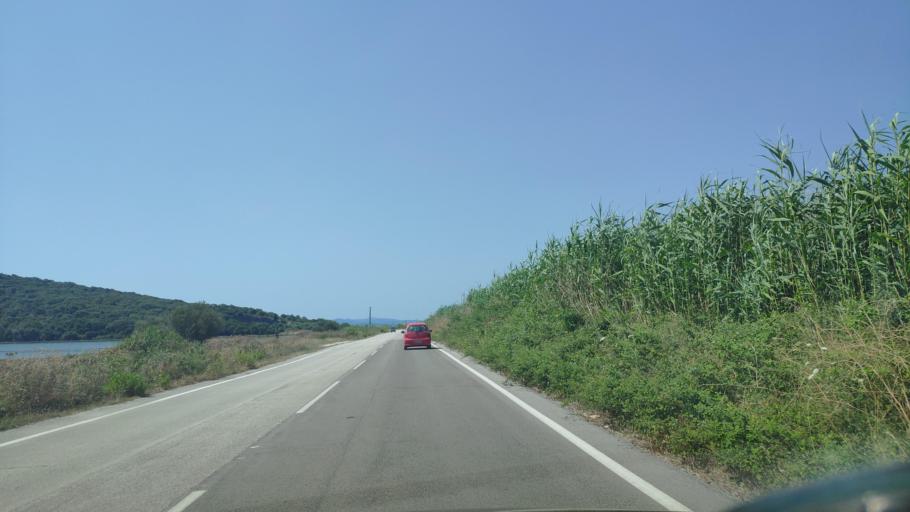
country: GR
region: Epirus
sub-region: Nomos Artas
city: Aneza
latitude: 39.0464
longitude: 20.8611
